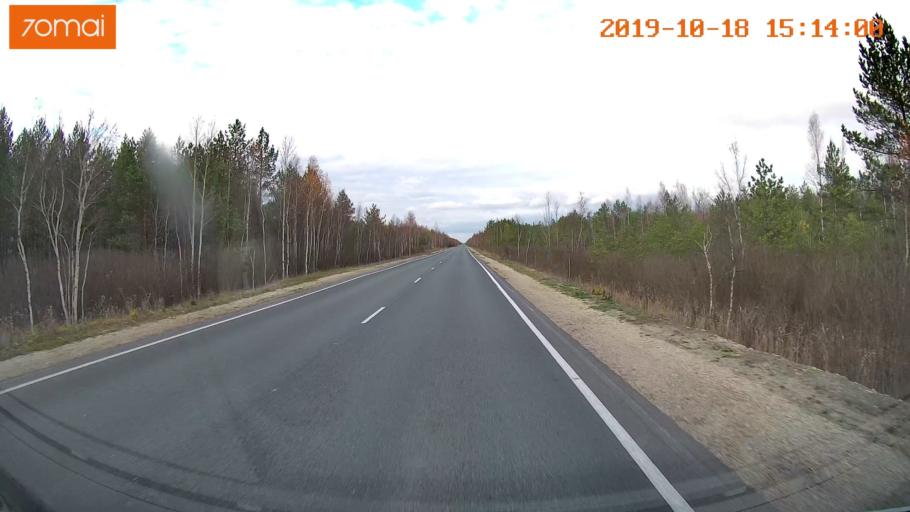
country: RU
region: Vladimir
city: Gus'-Khrustal'nyy
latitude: 55.5956
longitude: 40.7194
